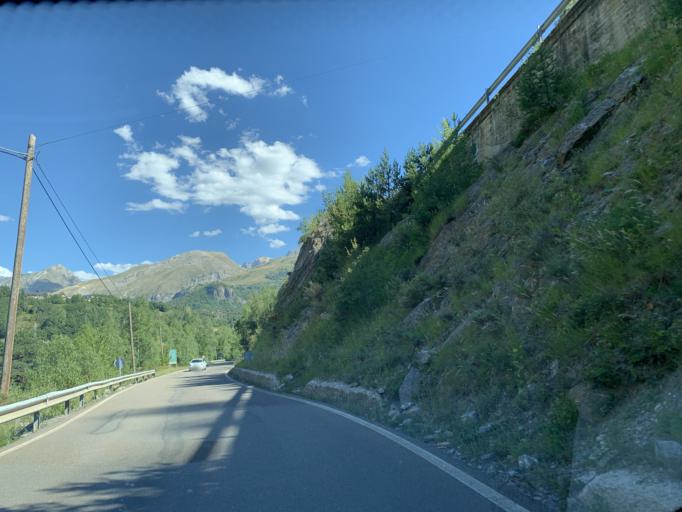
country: ES
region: Aragon
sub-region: Provincia de Huesca
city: Hoz de Jaca
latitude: 42.7286
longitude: -0.3091
